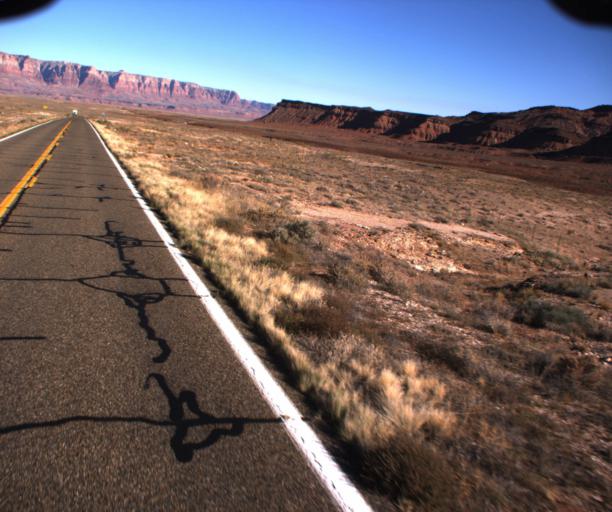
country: US
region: Arizona
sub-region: Coconino County
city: LeChee
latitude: 36.6831
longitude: -111.6542
